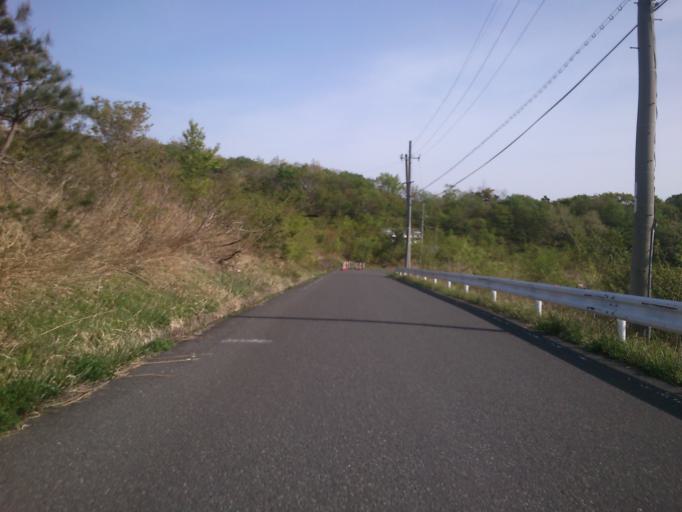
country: JP
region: Kyoto
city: Miyazu
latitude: 35.6547
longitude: 135.1810
